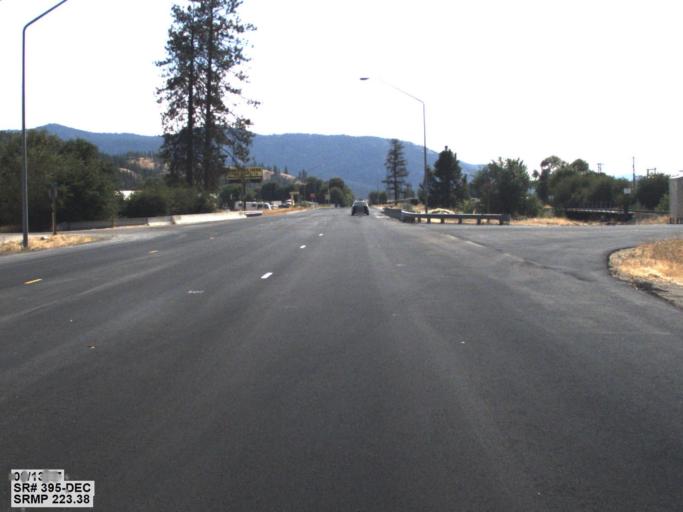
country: US
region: Washington
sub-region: Stevens County
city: Colville
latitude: 48.4604
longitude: -117.8821
